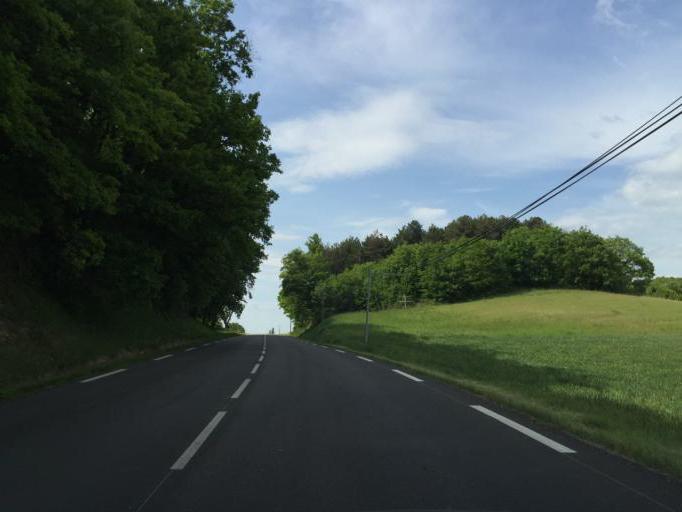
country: FR
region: Rhone-Alpes
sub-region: Departement de la Drome
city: Eurre
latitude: 44.7876
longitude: 5.0239
